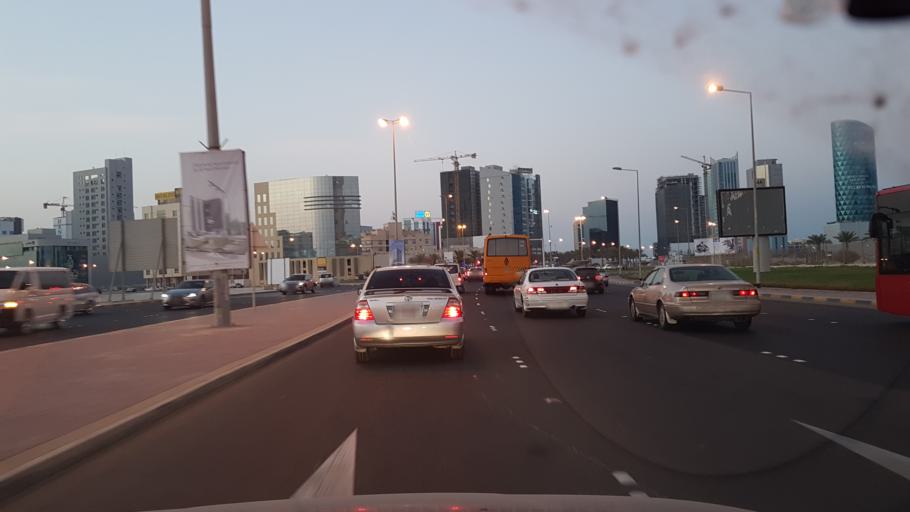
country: BH
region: Manama
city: Jidd Hafs
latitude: 26.2332
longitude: 50.5339
